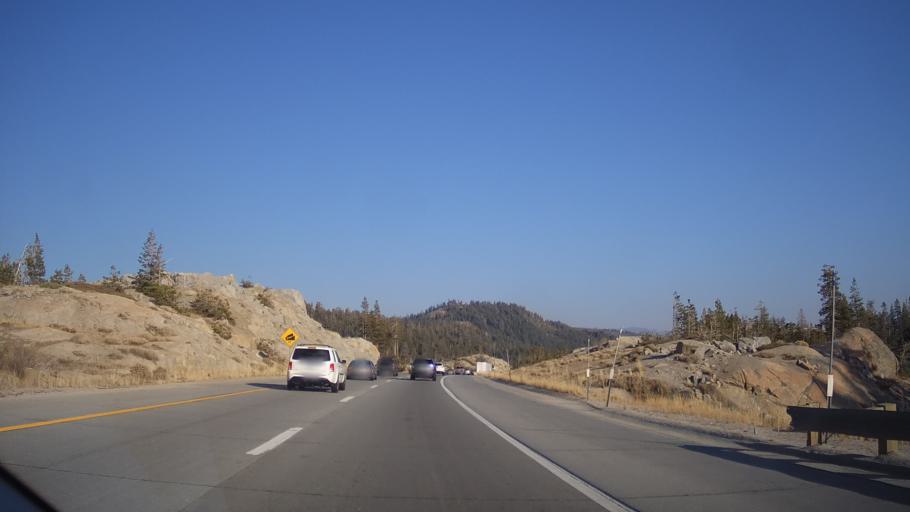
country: US
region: California
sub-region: Nevada County
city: Truckee
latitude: 39.3426
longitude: -120.3357
